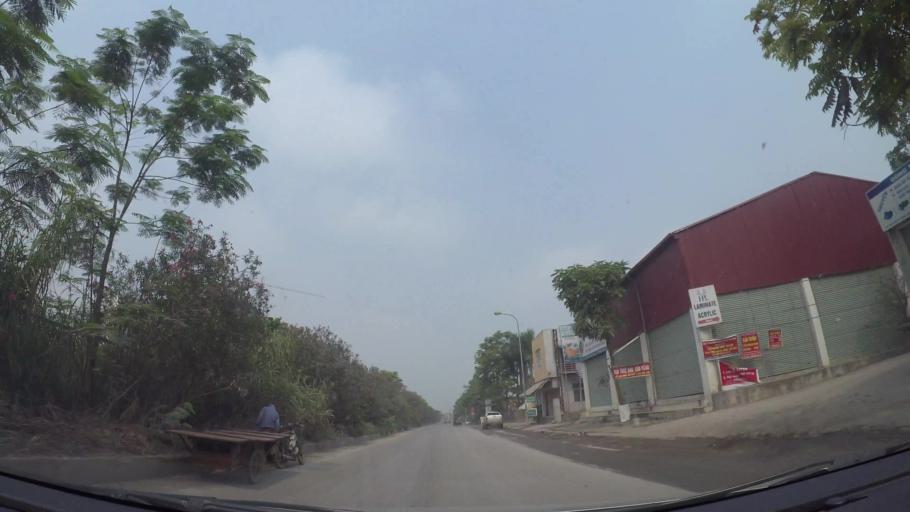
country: VN
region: Ha Noi
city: Cau Dien
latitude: 21.0114
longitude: 105.7251
